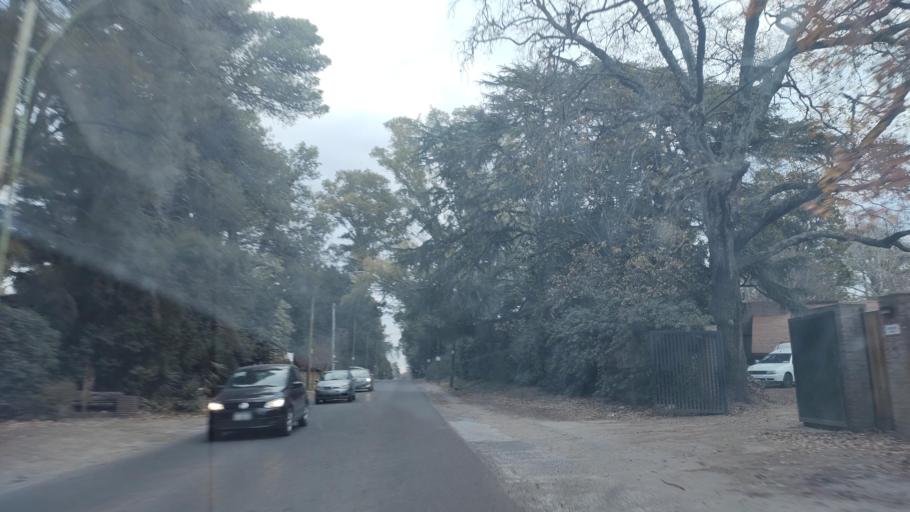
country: AR
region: Buenos Aires
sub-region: Partido de La Plata
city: La Plata
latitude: -34.8601
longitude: -58.0868
